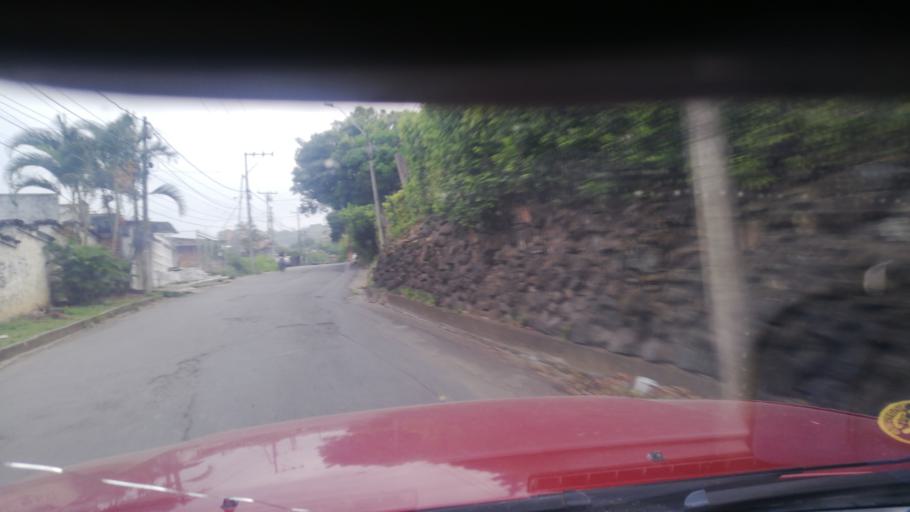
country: CO
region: Valle del Cauca
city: Cali
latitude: 3.4804
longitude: -76.5533
